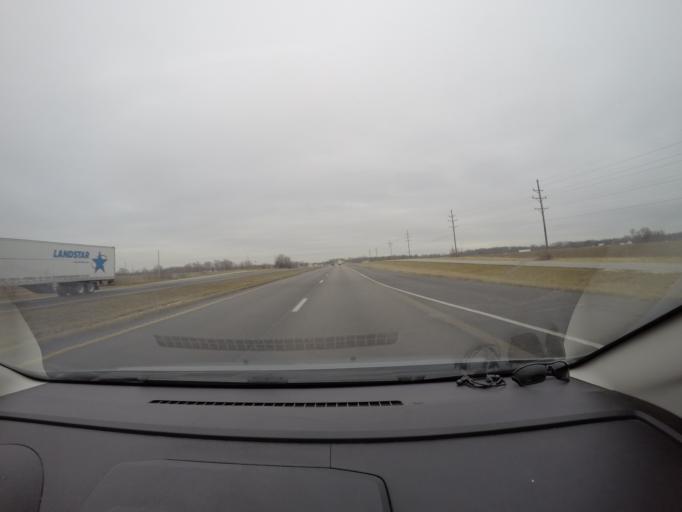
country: US
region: Missouri
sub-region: Warren County
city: Warrenton
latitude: 38.8355
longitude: -91.2209
